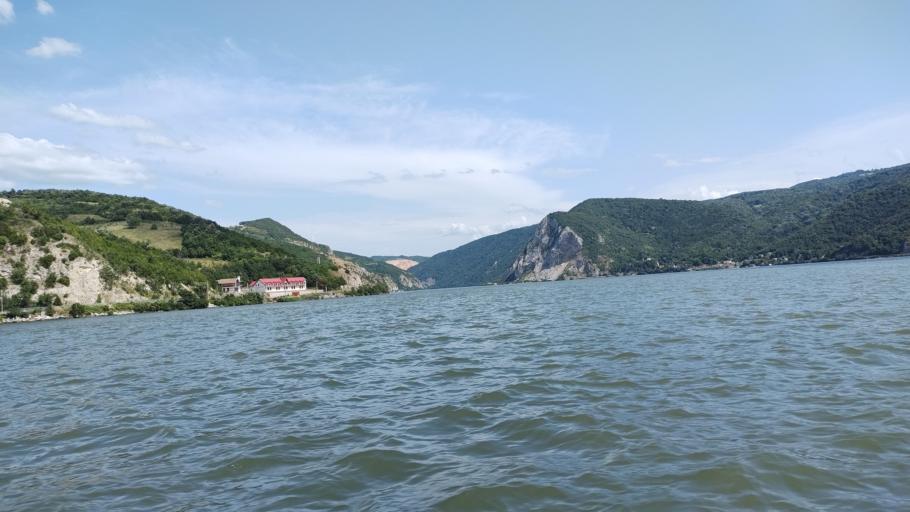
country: RO
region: Caras-Severin
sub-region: Comuna Pescari
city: Coronini
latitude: 44.6729
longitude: 21.6758
